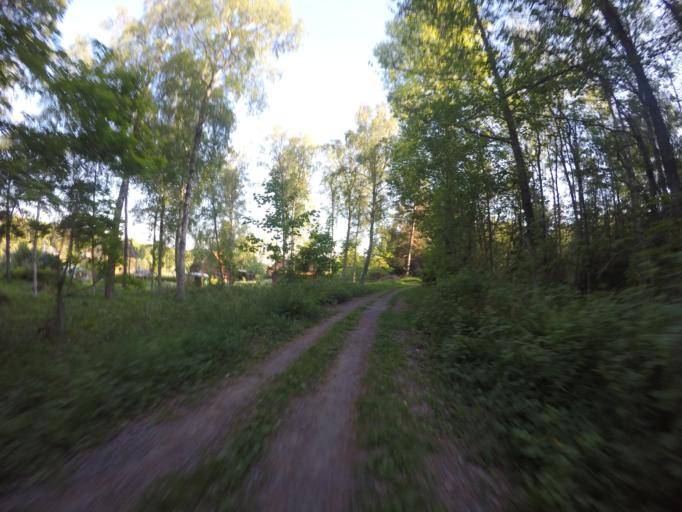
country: SE
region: Soedermanland
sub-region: Eskilstuna Kommun
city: Eskilstuna
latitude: 59.3415
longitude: 16.5277
